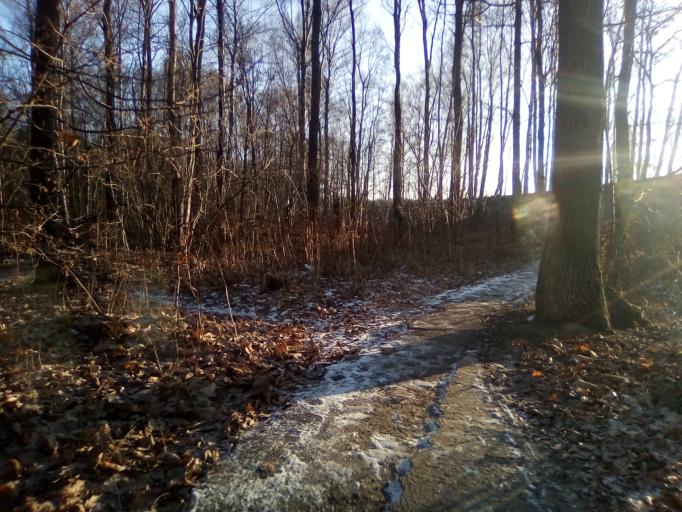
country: RU
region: Moskovskaya
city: Kokoshkino
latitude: 55.6477
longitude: 37.1565
